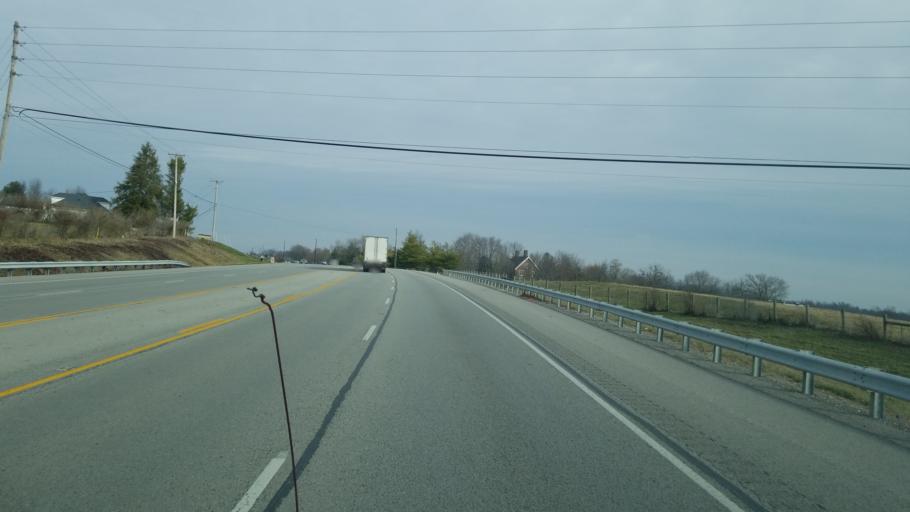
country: US
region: Kentucky
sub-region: Boyle County
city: Junction City
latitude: 37.5980
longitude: -84.7747
